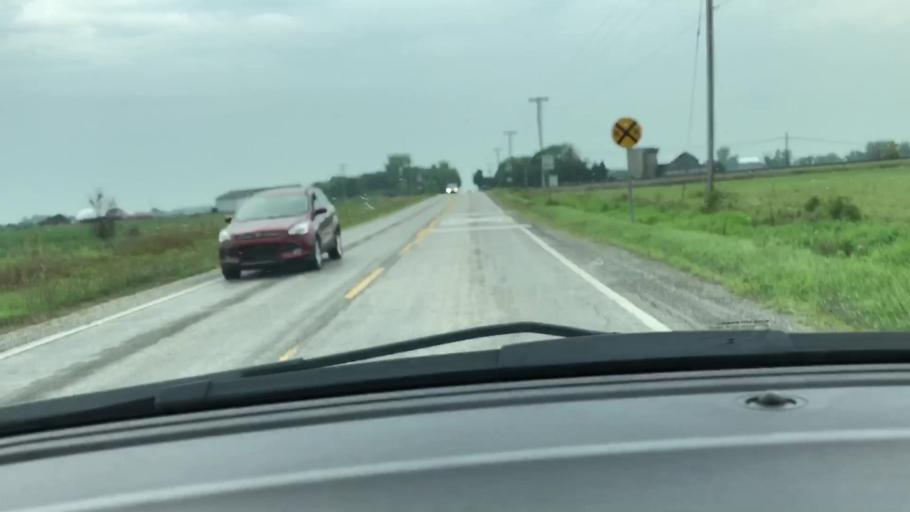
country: US
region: Michigan
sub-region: Saginaw County
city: Freeland
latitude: 43.5103
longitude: -84.0909
